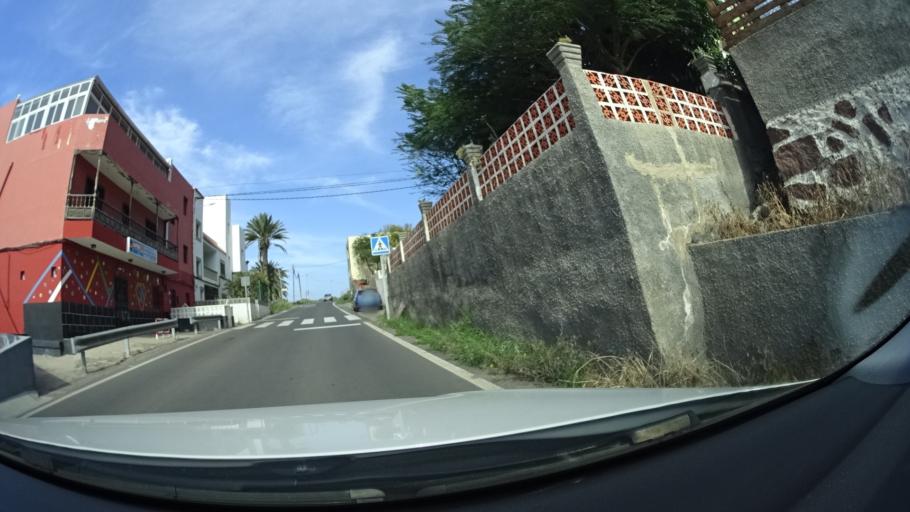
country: ES
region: Canary Islands
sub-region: Provincia de Las Palmas
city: Agaete
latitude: 28.1105
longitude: -15.6657
